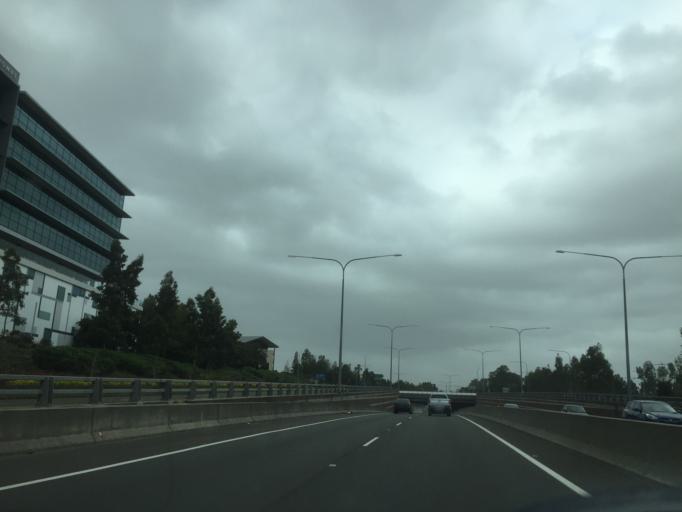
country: AU
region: New South Wales
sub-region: Blacktown
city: Stanhope Gardens
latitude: -33.7389
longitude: 150.9462
